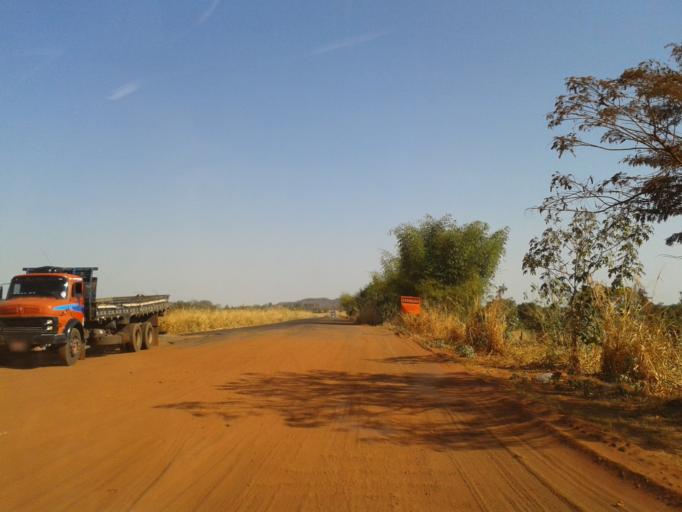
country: BR
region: Minas Gerais
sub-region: Ituiutaba
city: Ituiutaba
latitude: -19.0026
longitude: -49.4912
